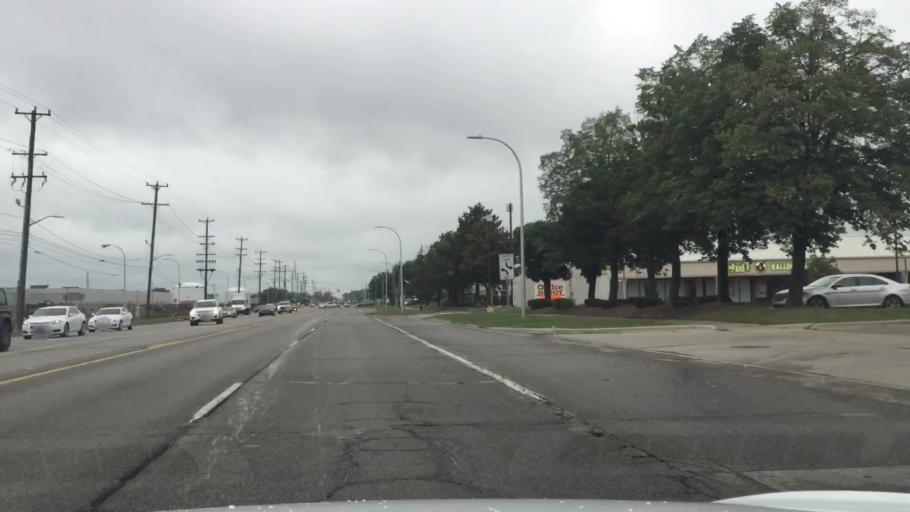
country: US
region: Michigan
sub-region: Wayne County
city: Livonia
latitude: 42.3699
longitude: -83.3330
